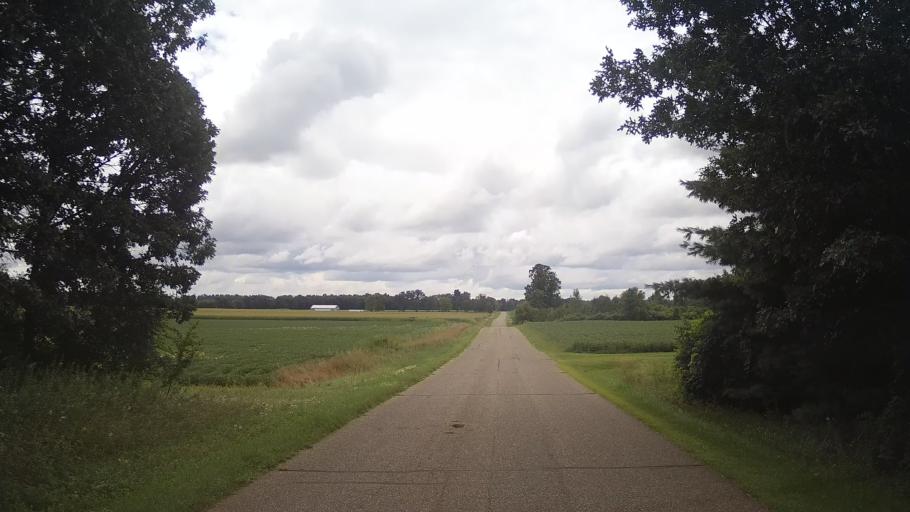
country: US
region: Wisconsin
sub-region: Adams County
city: Friendship
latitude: 44.0350
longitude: -89.9177
